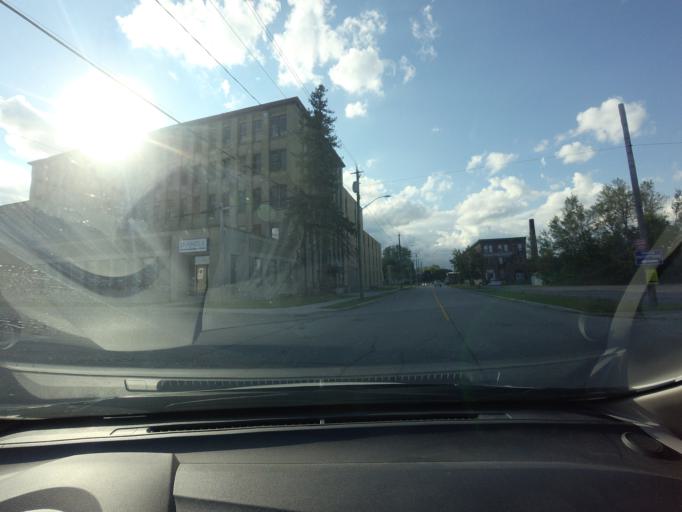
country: CA
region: Ontario
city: Perth
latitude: 44.9028
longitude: -76.2457
